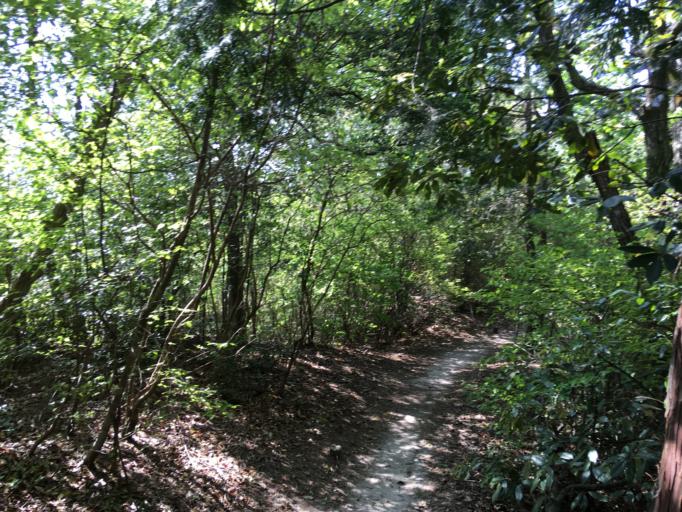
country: JP
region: Nara
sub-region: Ikoma-shi
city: Ikoma
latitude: 34.6956
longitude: 135.7171
